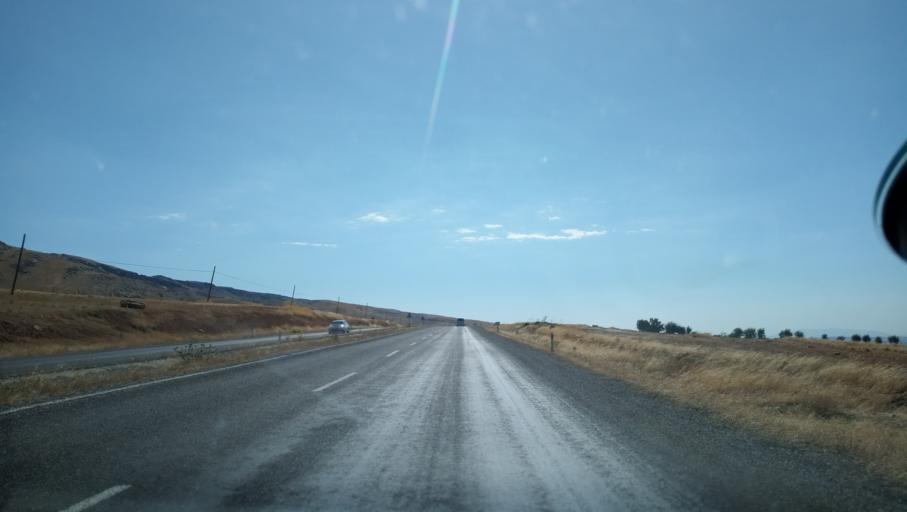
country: TR
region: Diyarbakir
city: Silvan
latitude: 38.1280
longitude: 41.0671
